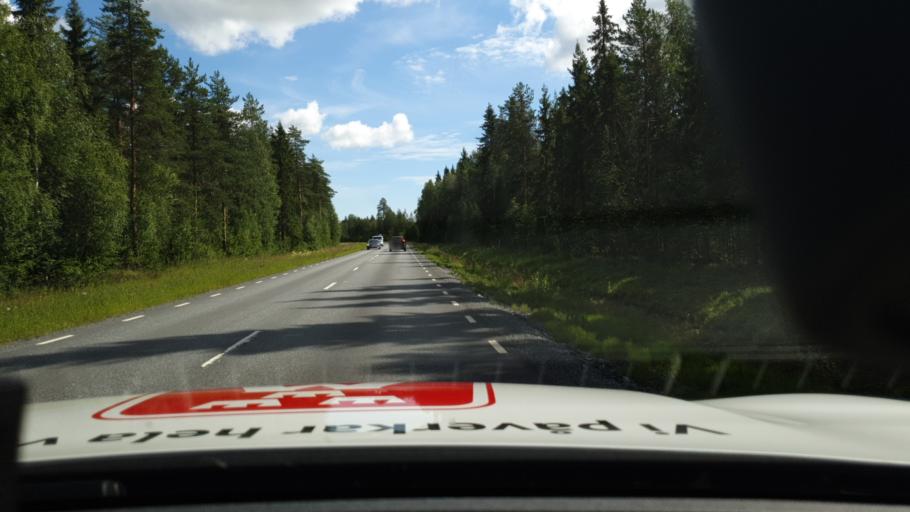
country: SE
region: Norrbotten
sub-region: Lulea Kommun
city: Gammelstad
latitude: 65.7873
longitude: 22.0980
